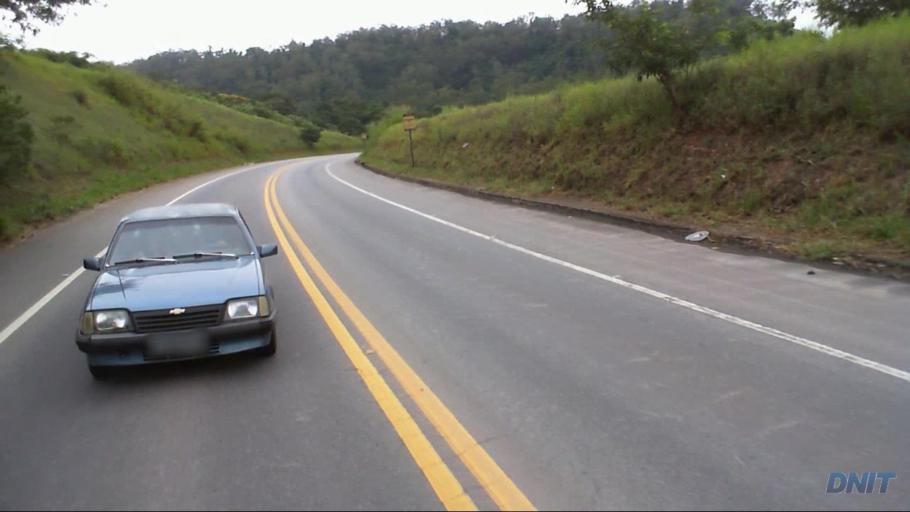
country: BR
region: Minas Gerais
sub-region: Coronel Fabriciano
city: Coronel Fabriciano
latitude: -19.5225
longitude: -42.5815
